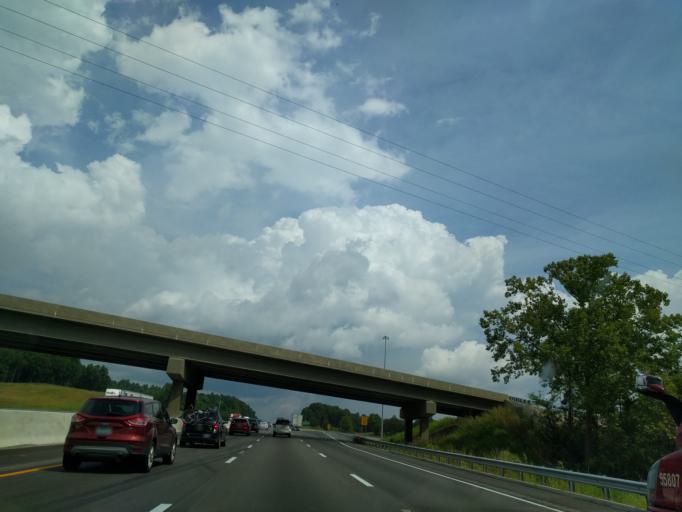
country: US
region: Kentucky
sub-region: Hart County
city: Munfordville
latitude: 37.3786
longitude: -85.8887
